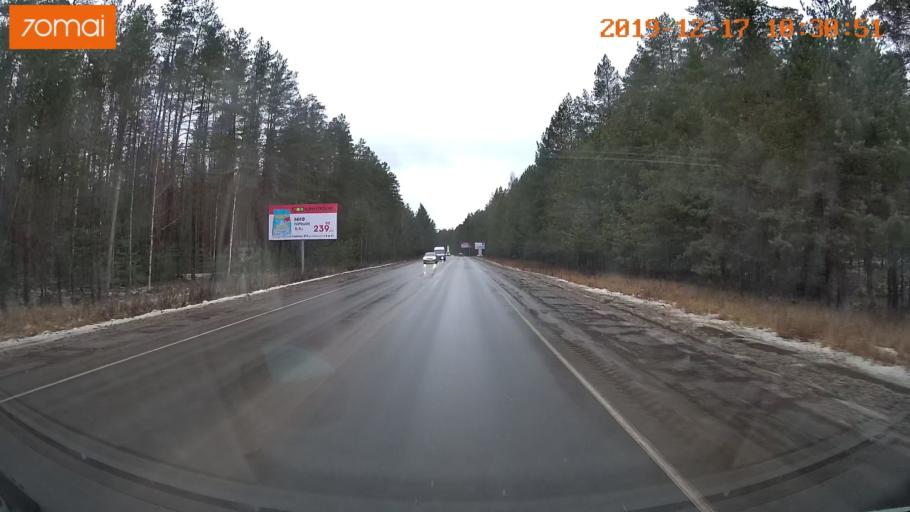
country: RU
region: Vladimir
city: Gus'-Khrustal'nyy
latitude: 55.6397
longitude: 40.7037
